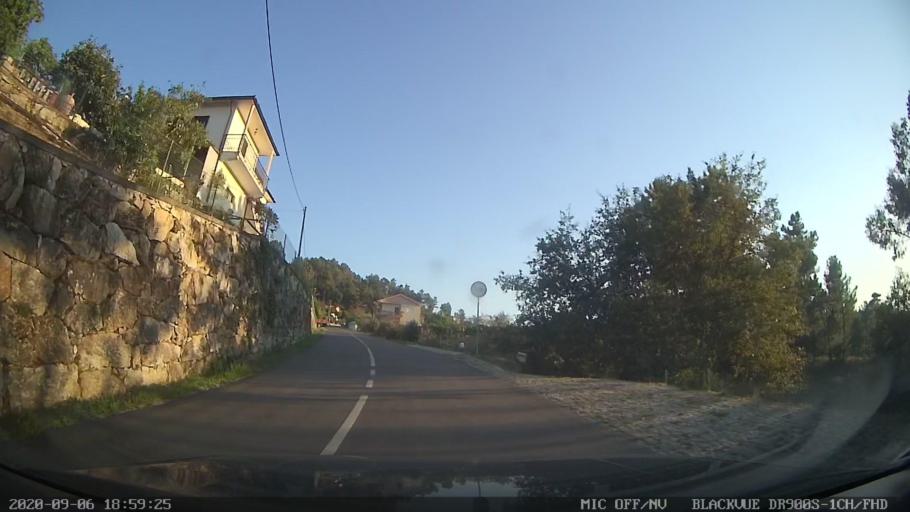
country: PT
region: Porto
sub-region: Baiao
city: Baiao
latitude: 41.2431
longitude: -7.9964
